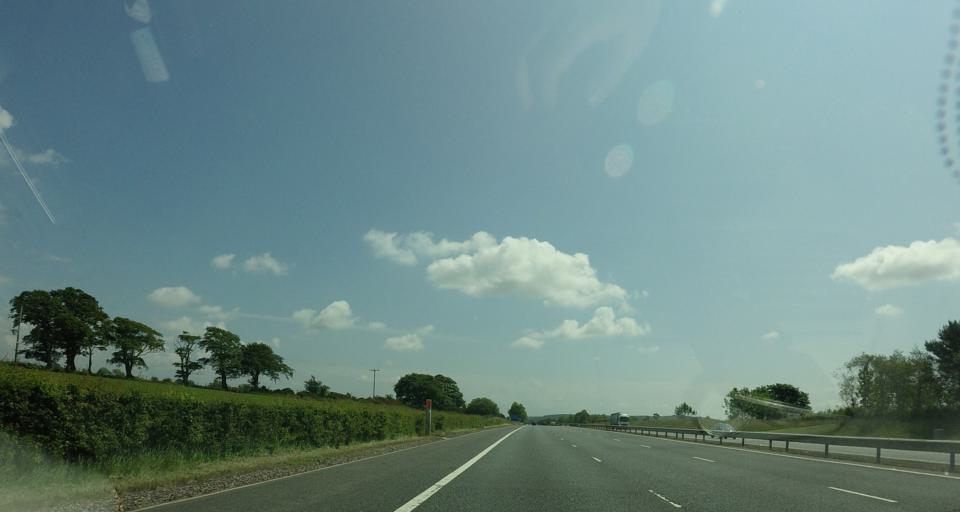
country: GB
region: Scotland
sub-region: Dumfries and Galloway
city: Lockerbie
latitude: 55.0713
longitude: -3.2943
